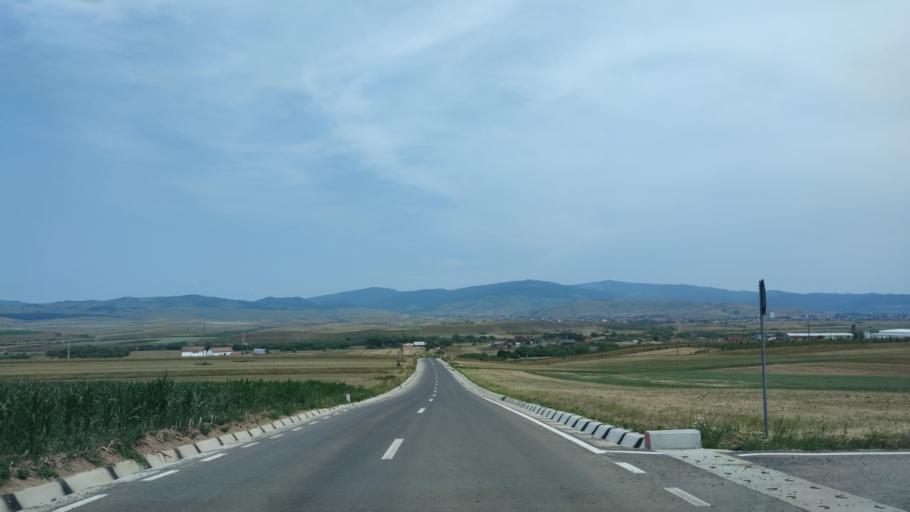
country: RO
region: Harghita
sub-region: Comuna Subcetate
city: Subcetate
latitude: 46.8180
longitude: 25.4507
